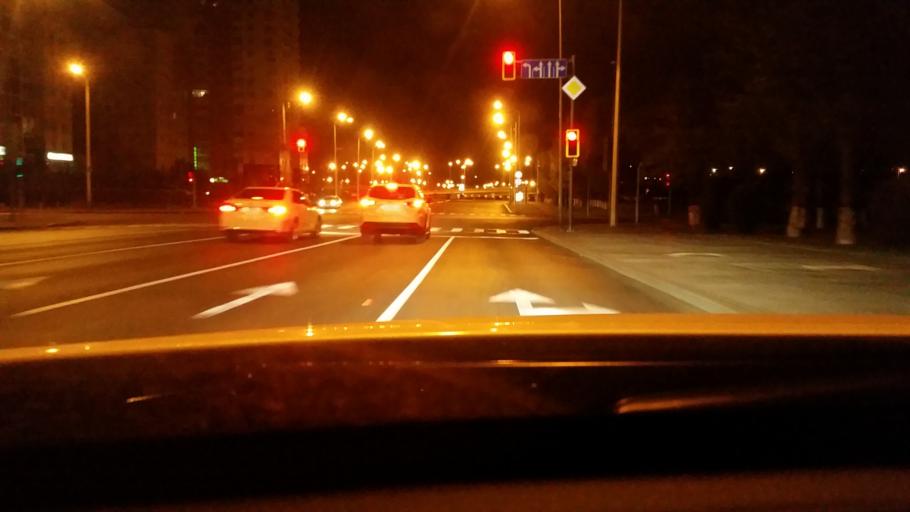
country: KZ
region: Astana Qalasy
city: Astana
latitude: 51.1289
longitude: 71.4393
